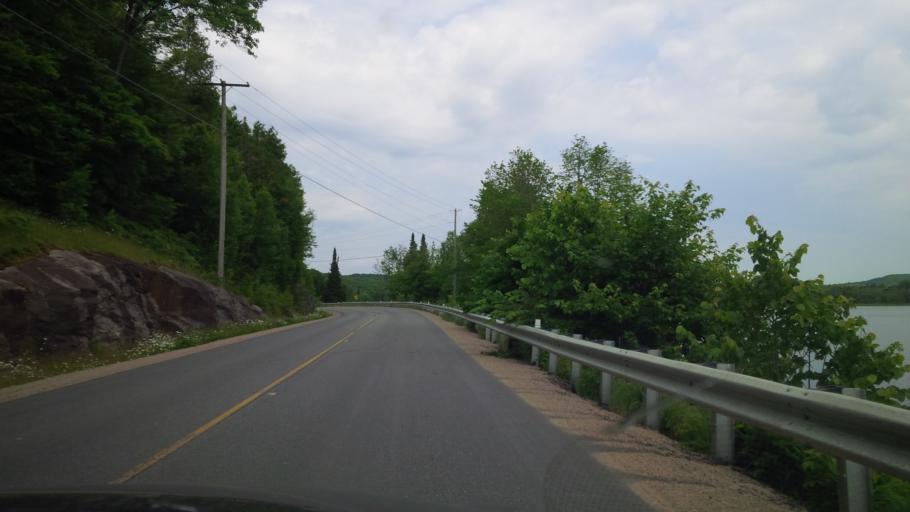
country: CA
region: Ontario
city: Huntsville
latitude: 45.5803
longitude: -79.2160
